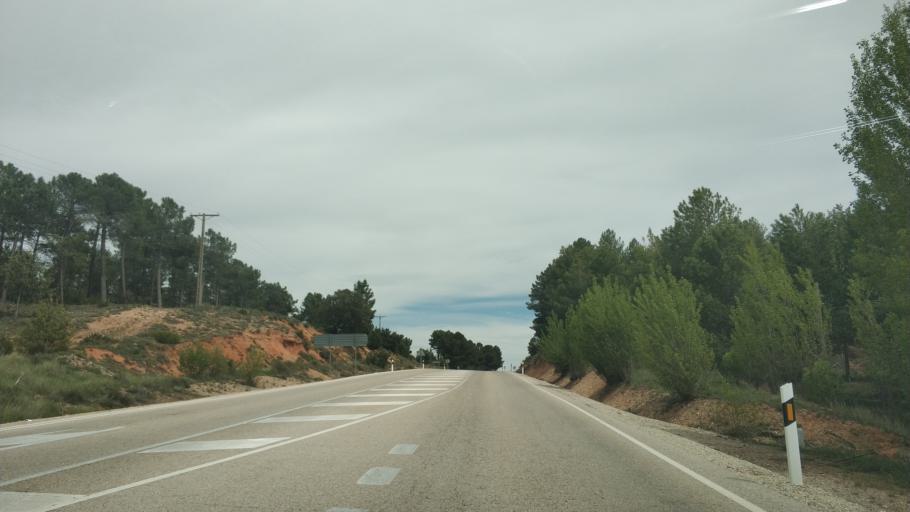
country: ES
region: Castille and Leon
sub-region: Provincia de Soria
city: Valdenebro
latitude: 41.5593
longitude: -2.9717
